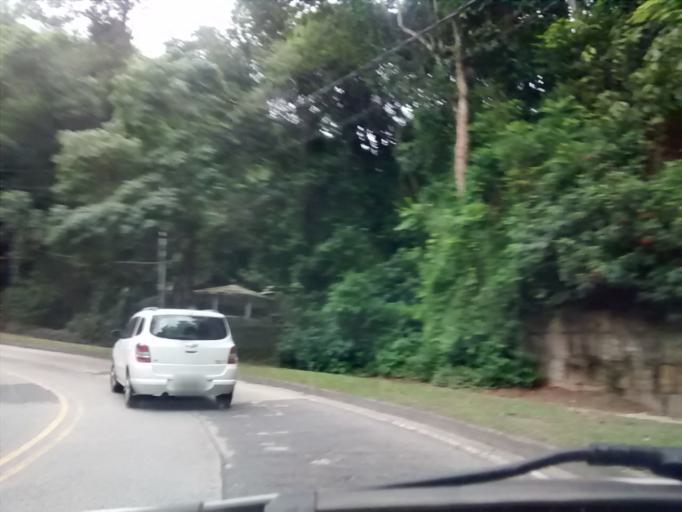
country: BR
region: Rio de Janeiro
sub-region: Rio De Janeiro
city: Rio de Janeiro
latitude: -22.9571
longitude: -43.2688
